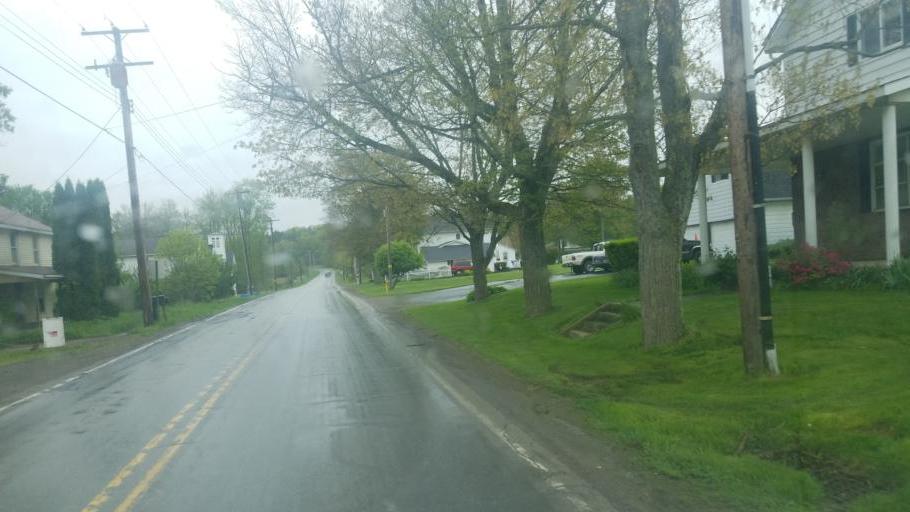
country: US
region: Pennsylvania
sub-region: Forest County
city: Tionesta
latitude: 41.3857
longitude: -79.3219
